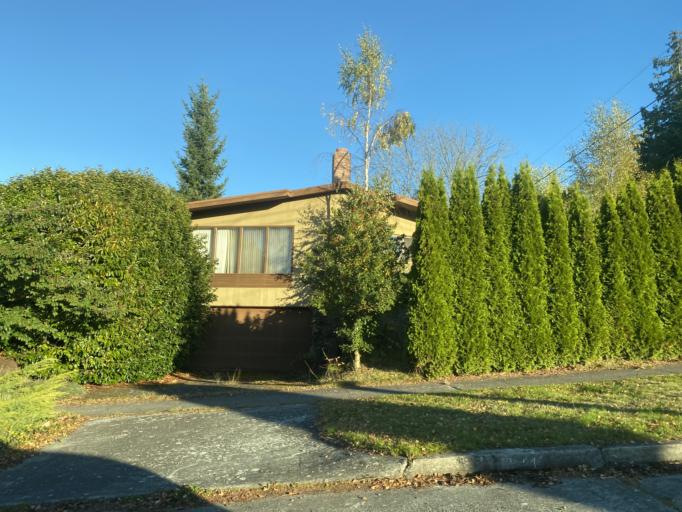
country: US
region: Washington
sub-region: King County
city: Seattle
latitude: 47.6516
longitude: -122.3956
